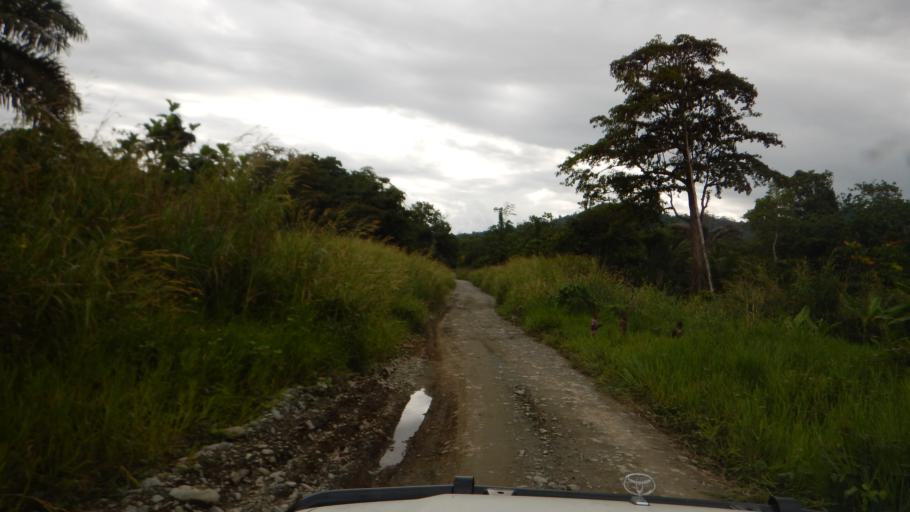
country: PG
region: Northern Province
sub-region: Sohe
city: Kokoda
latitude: -8.9183
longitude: 147.8644
